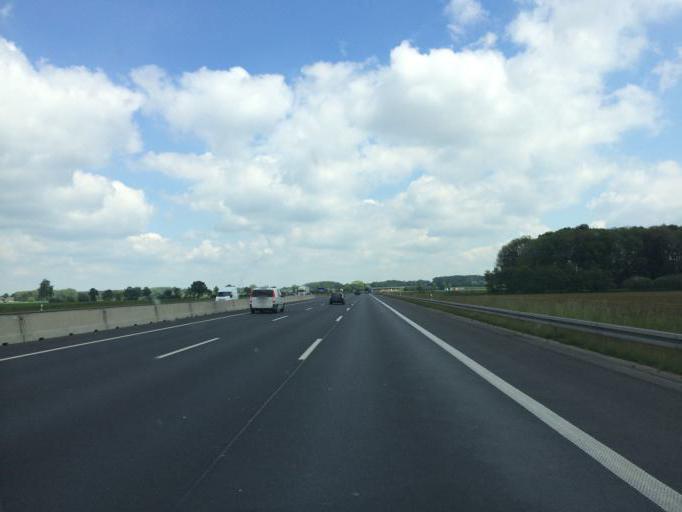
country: DE
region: North Rhine-Westphalia
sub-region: Regierungsbezirk Arnsberg
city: Bonen
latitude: 51.6212
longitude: 7.8057
